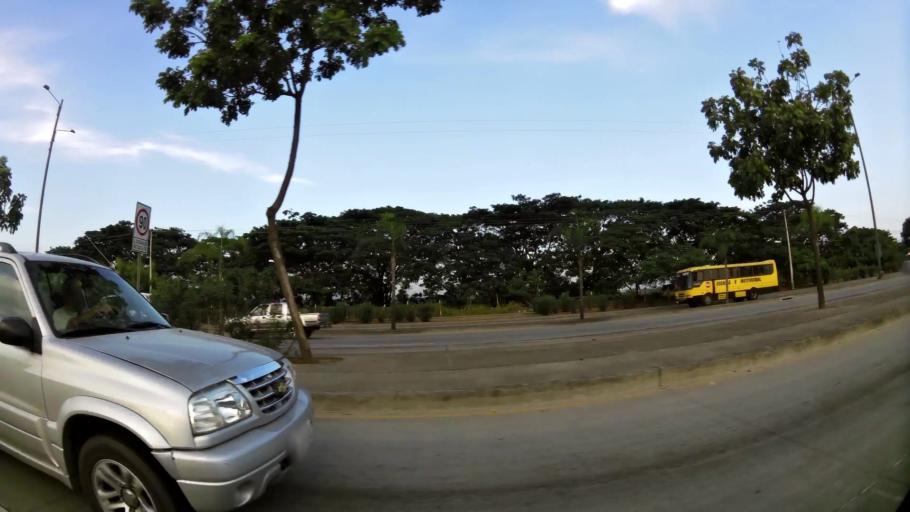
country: EC
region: Guayas
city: Eloy Alfaro
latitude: -2.0942
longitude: -79.8933
